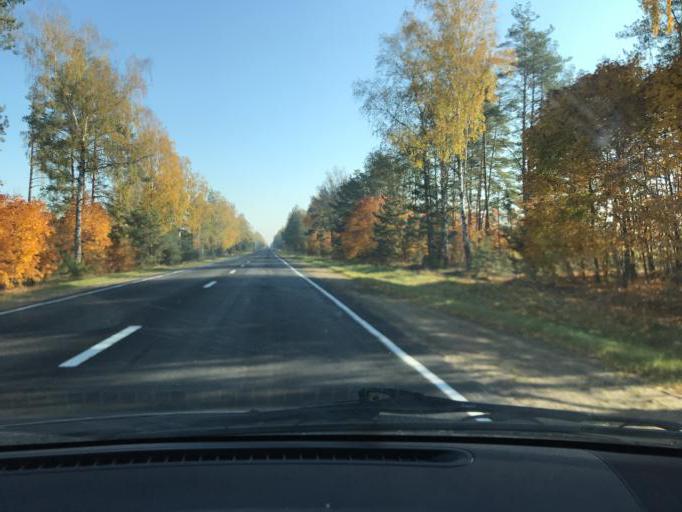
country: BY
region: Brest
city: Baranovichi
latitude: 52.9055
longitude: 25.9001
